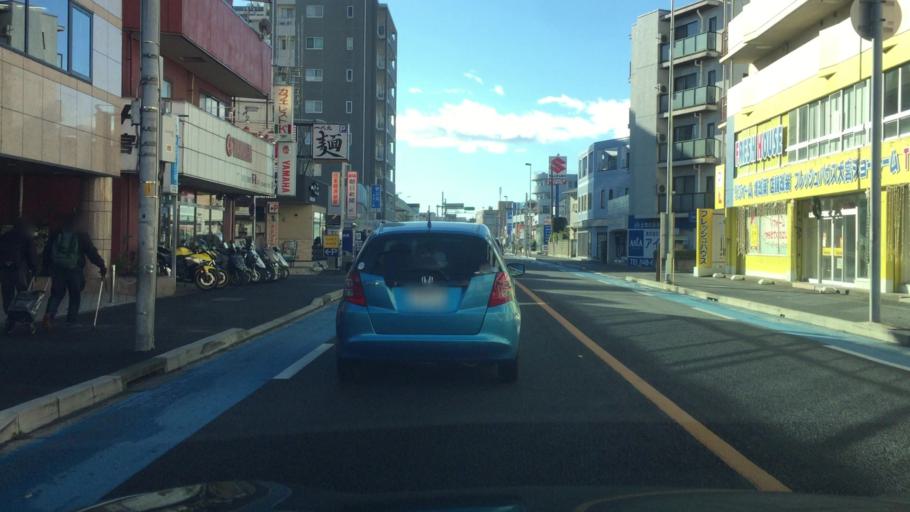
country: JP
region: Saitama
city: Yono
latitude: 35.9215
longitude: 139.6151
